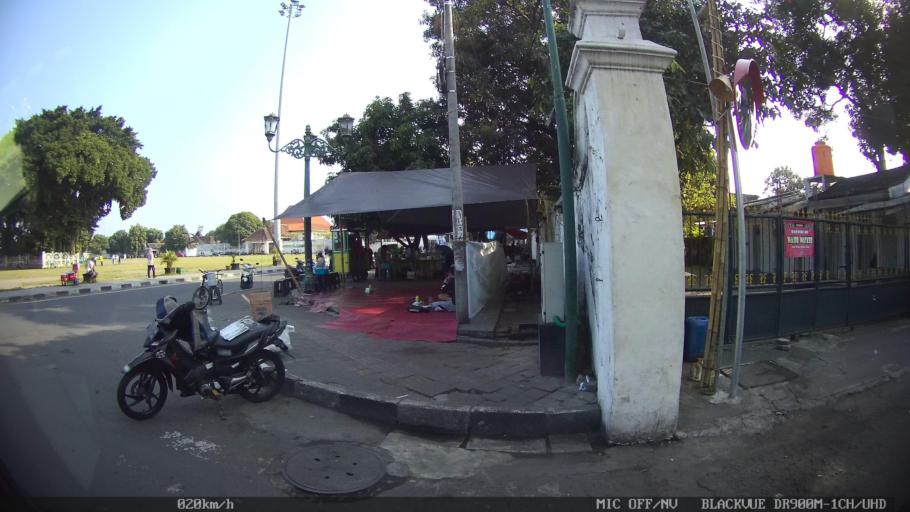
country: ID
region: Daerah Istimewa Yogyakarta
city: Yogyakarta
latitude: -7.8161
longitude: 110.3706
